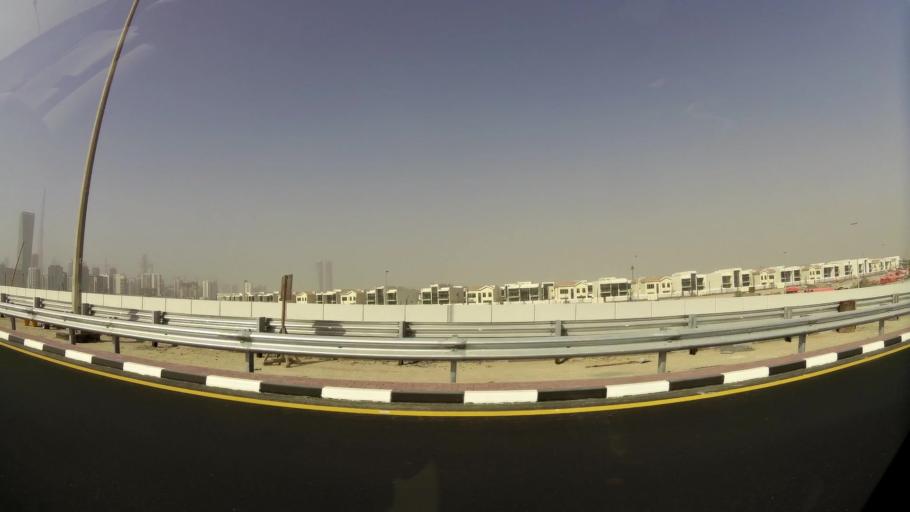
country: AE
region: Dubai
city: Dubai
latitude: 25.1663
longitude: 55.2697
